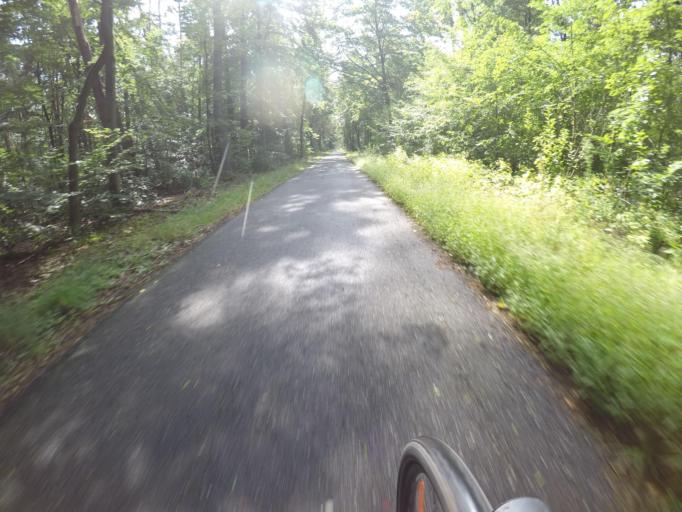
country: DE
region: Baden-Wuerttemberg
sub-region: Karlsruhe Region
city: Reilingen
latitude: 49.3184
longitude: 8.6005
